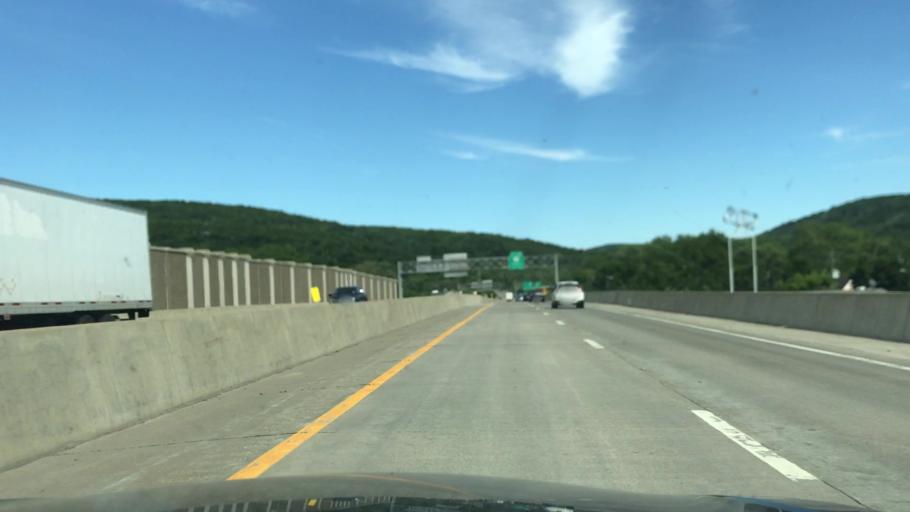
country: US
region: New York
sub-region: Chemung County
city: Horseheads
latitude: 42.1558
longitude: -76.8161
